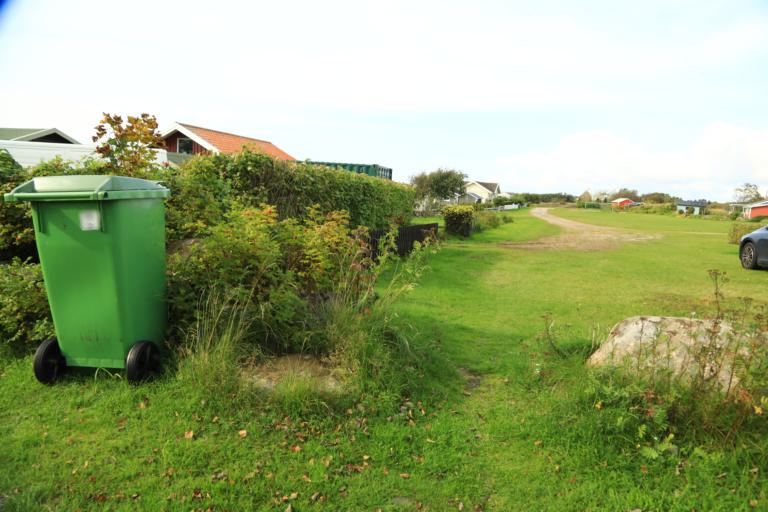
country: SE
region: Halland
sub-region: Varbergs Kommun
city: Tvaaker
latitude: 57.0218
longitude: 12.3378
